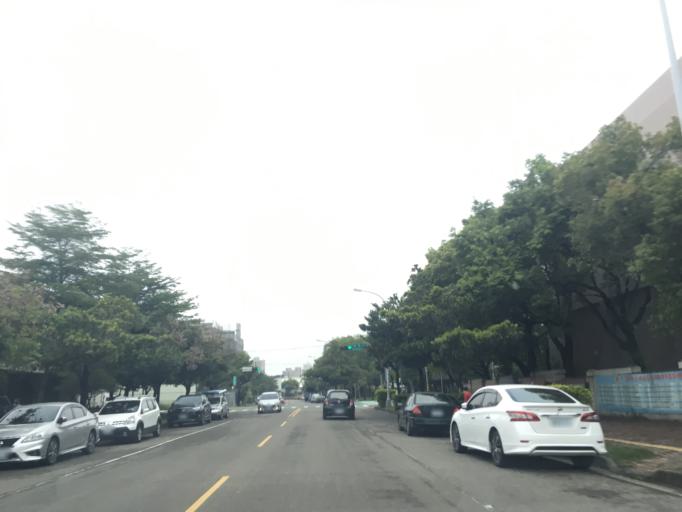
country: TW
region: Taiwan
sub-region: Taichung City
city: Taichung
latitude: 24.1665
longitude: 120.7119
